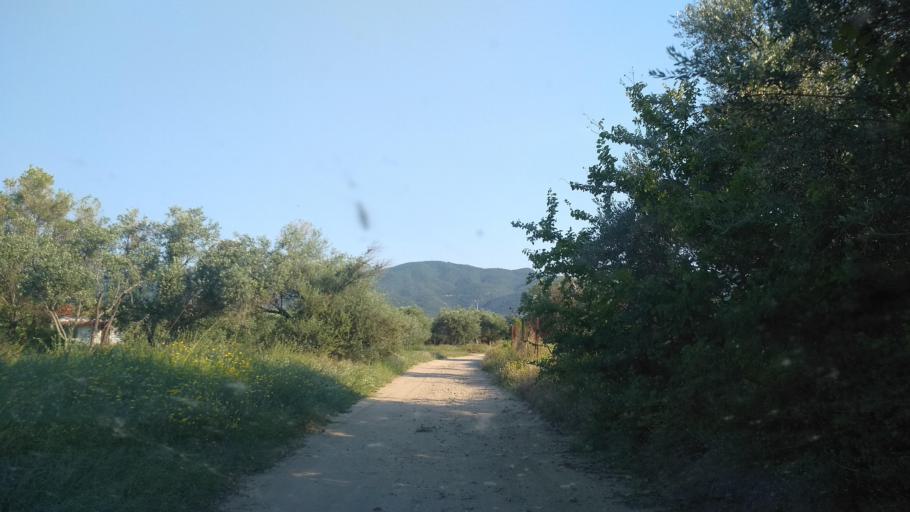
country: GR
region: Central Macedonia
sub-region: Nomos Thessalonikis
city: Nea Vrasna
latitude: 40.6880
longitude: 23.6825
